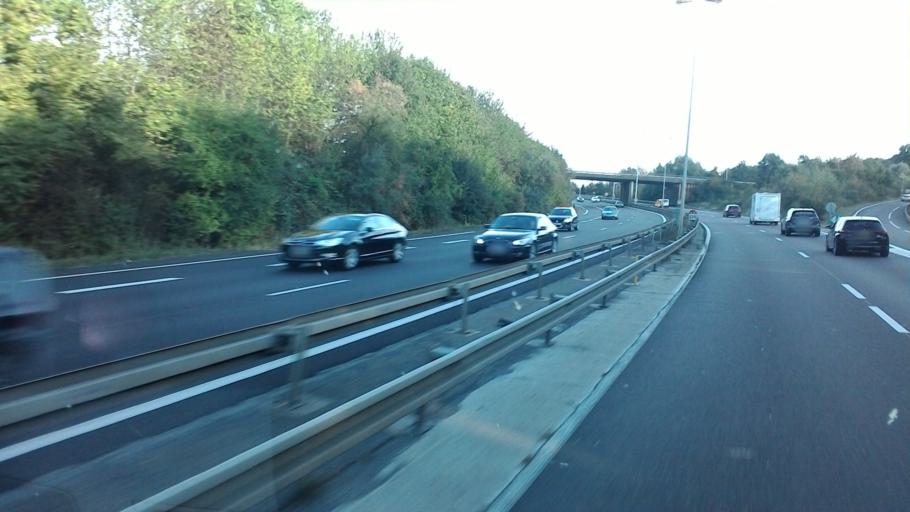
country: FR
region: Lorraine
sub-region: Departement de la Moselle
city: Florange
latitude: 49.3477
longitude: 6.1106
